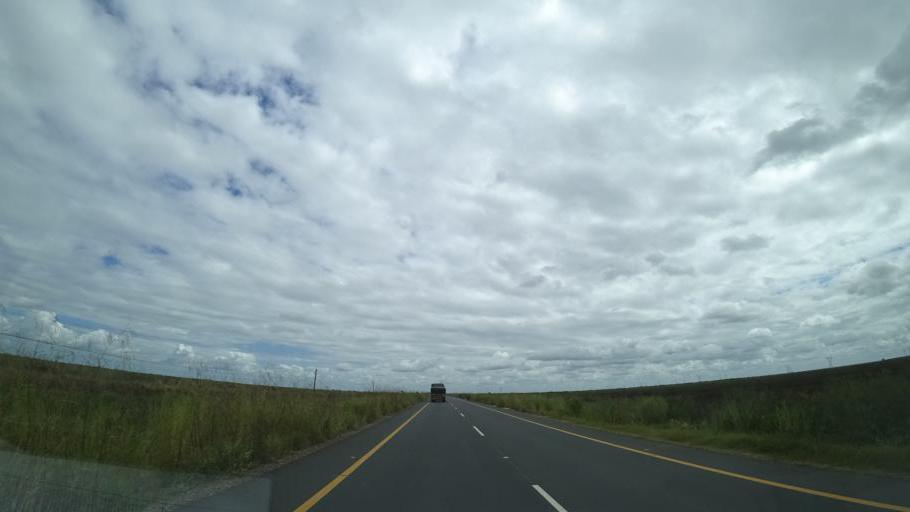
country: MZ
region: Sofala
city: Dondo
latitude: -19.4853
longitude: 34.5779
